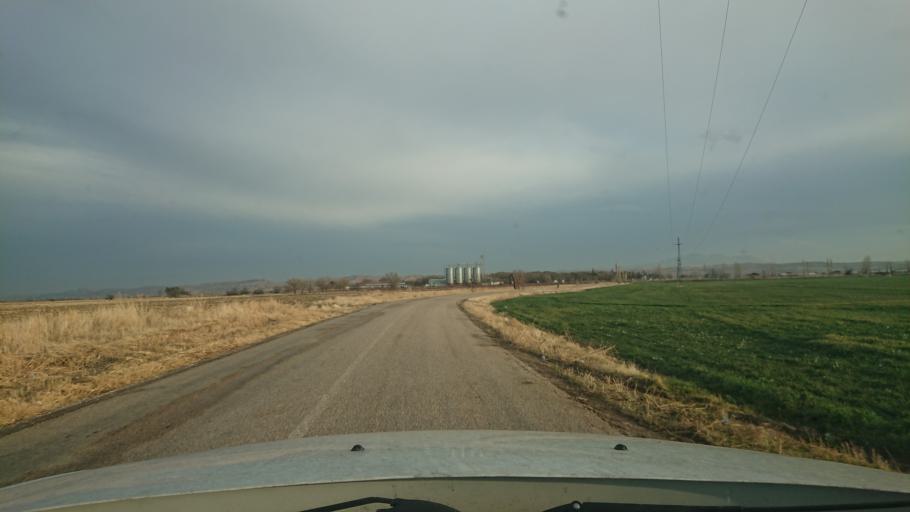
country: TR
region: Aksaray
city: Yesilova
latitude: 38.4508
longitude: 33.8347
